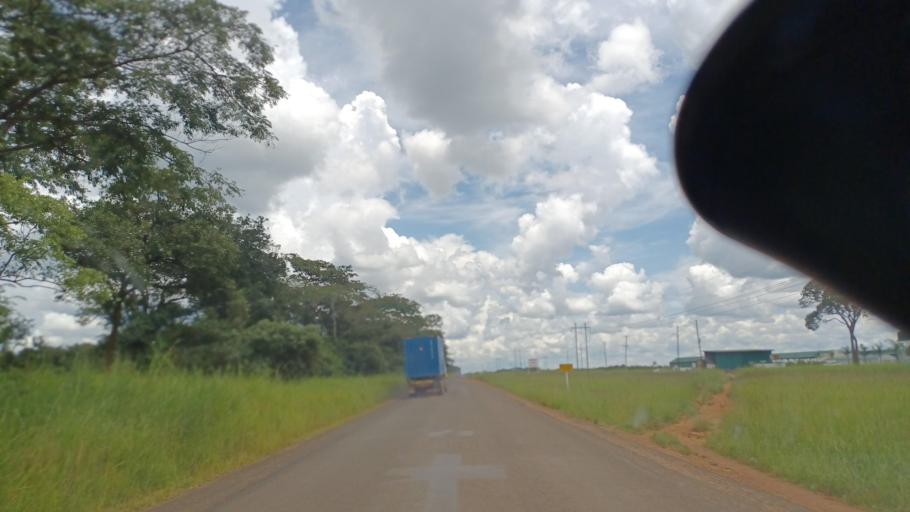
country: ZM
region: North-Western
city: Solwezi
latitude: -12.4372
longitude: 26.2101
